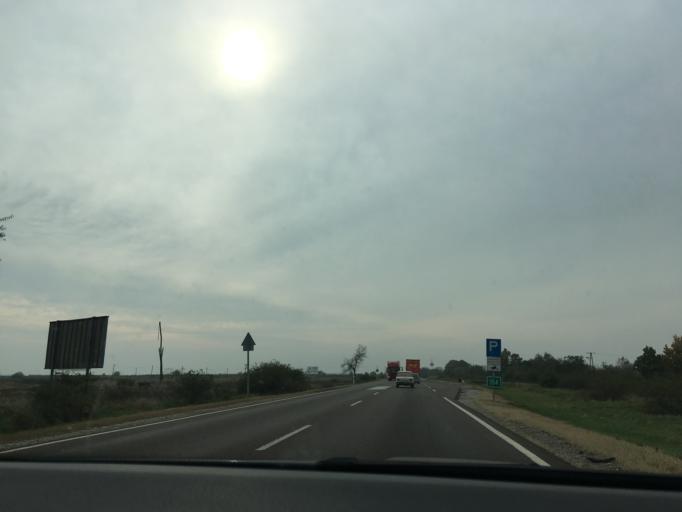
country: HU
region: Jasz-Nagykun-Szolnok
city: Kisujszallas
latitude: 47.2447
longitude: 20.8315
